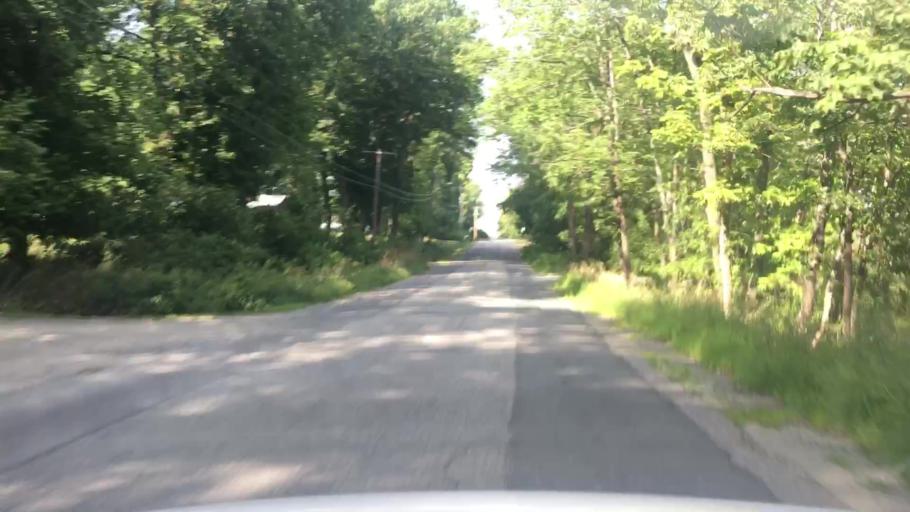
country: US
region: Maine
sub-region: Kennebec County
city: Waterville
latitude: 44.5711
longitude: -69.6669
